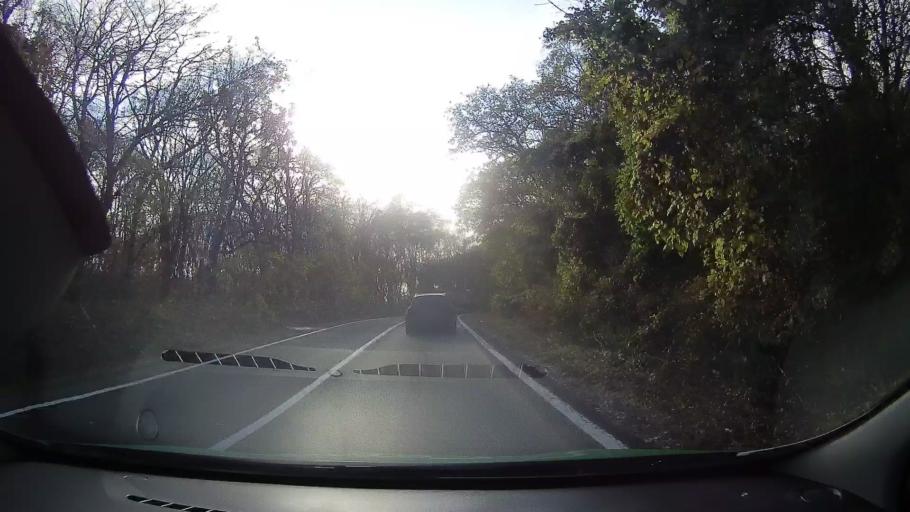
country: RO
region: Tulcea
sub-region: Comuna Topolog
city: Topolog
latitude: 44.9074
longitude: 28.4177
